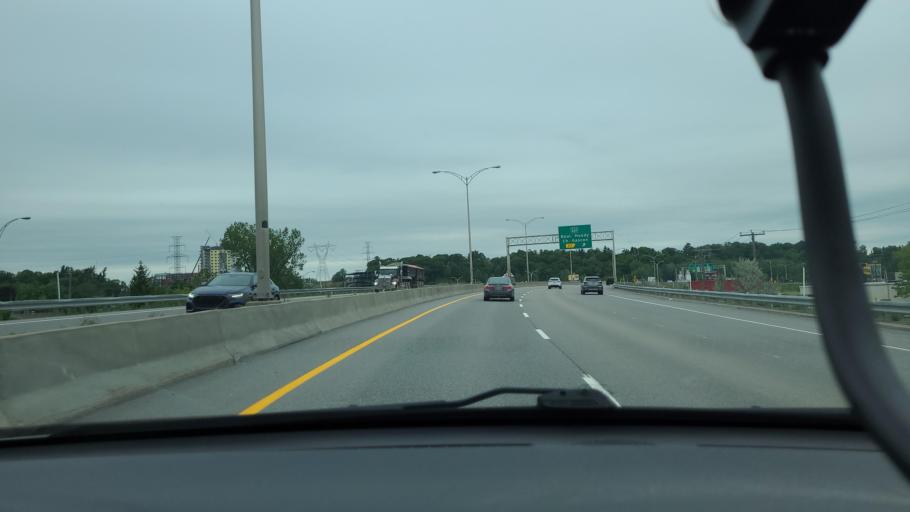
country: CA
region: Quebec
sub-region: Lanaudiere
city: Terrebonne
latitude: 45.7047
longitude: -73.6520
